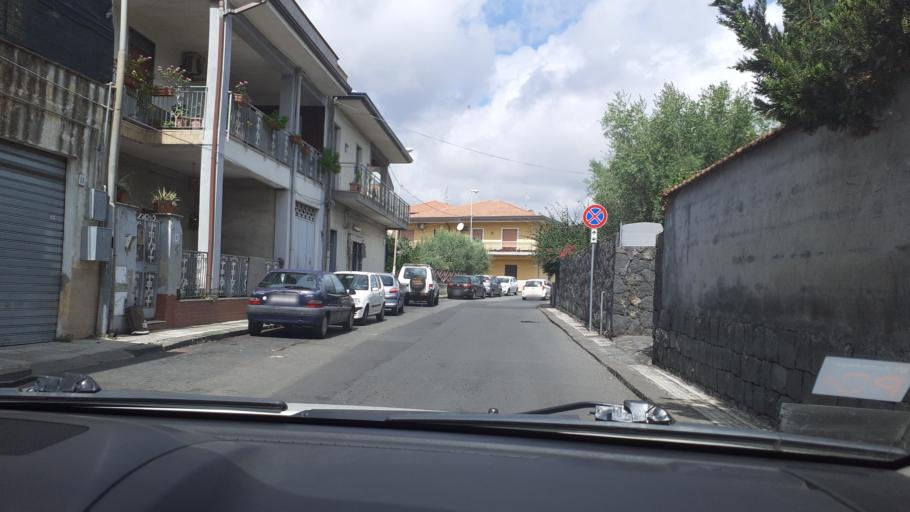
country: IT
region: Sicily
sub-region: Catania
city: San Giovanni la Punta
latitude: 37.5861
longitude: 15.0954
